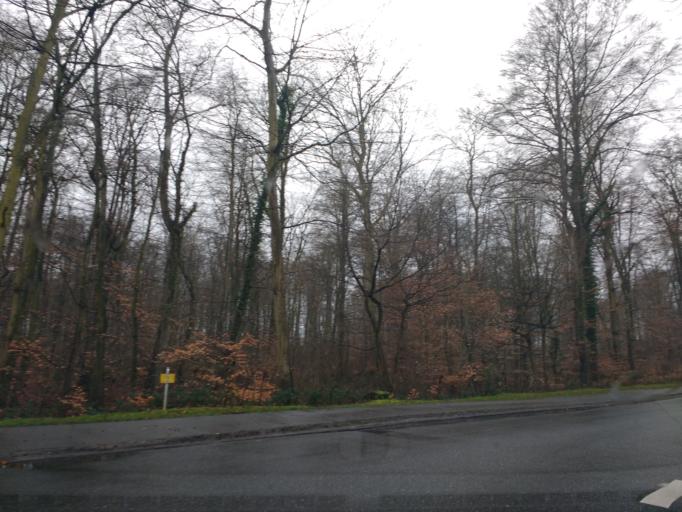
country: DE
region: Schleswig-Holstein
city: Blekendorf
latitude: 54.3209
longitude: 10.6621
